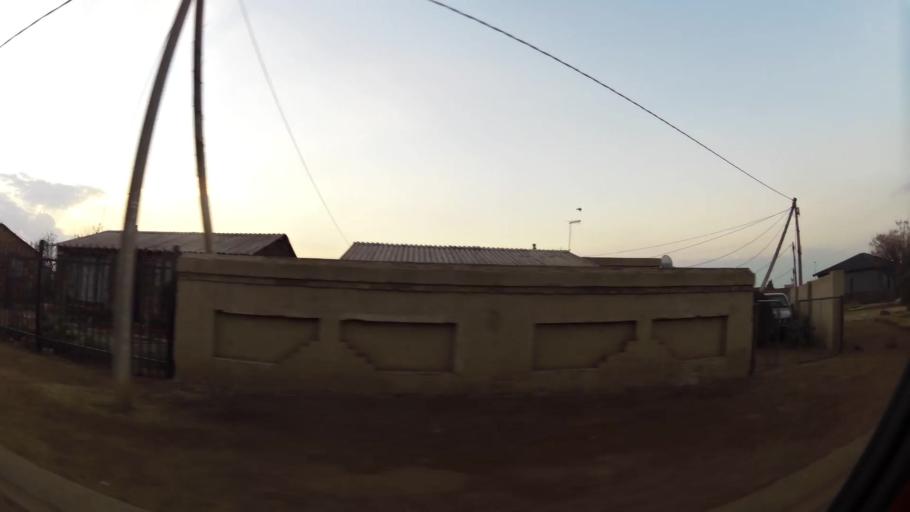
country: ZA
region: Gauteng
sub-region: City of Johannesburg Metropolitan Municipality
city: Orange Farm
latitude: -26.5514
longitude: 27.8810
